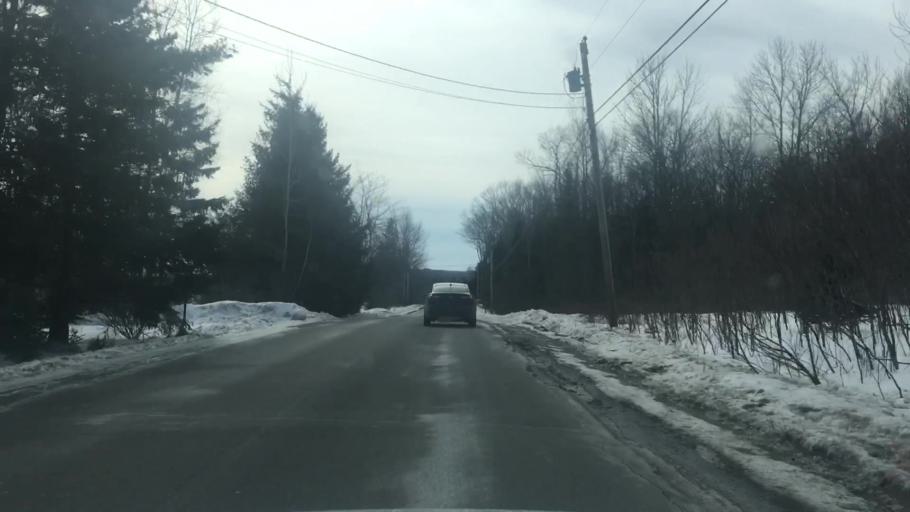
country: US
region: Maine
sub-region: Hancock County
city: Orland
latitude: 44.5999
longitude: -68.7218
